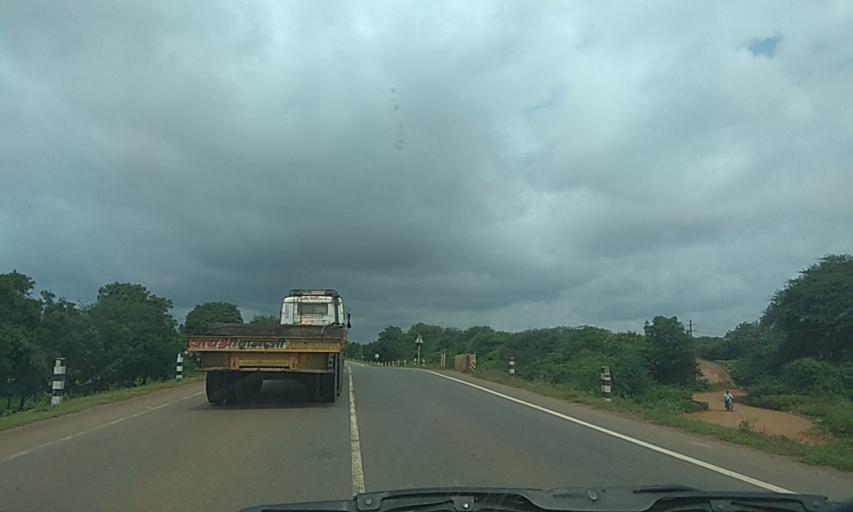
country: IN
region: Karnataka
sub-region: Dharwad
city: Hubli
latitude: 15.3353
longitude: 75.0938
